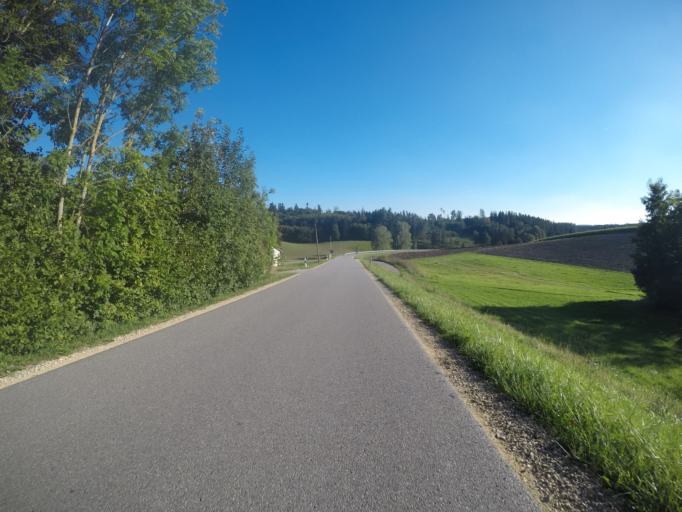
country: DE
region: Bavaria
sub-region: Lower Bavaria
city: Kumhausen
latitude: 48.5074
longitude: 12.1792
